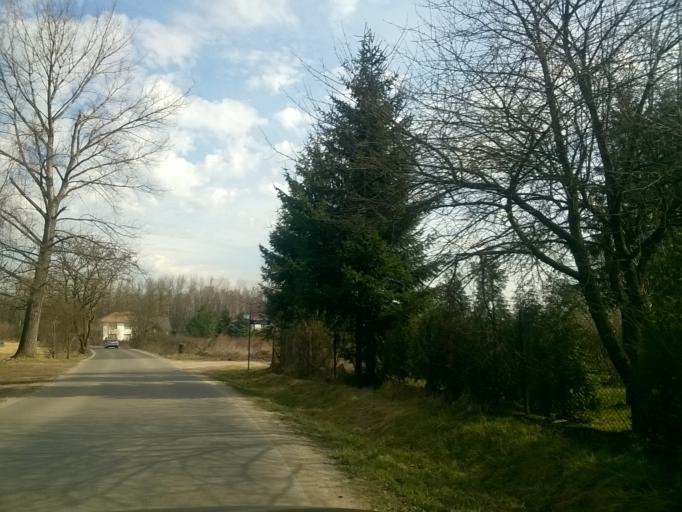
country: PL
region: Lesser Poland Voivodeship
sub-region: Powiat krakowski
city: Rzaska
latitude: 50.0896
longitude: 19.8644
